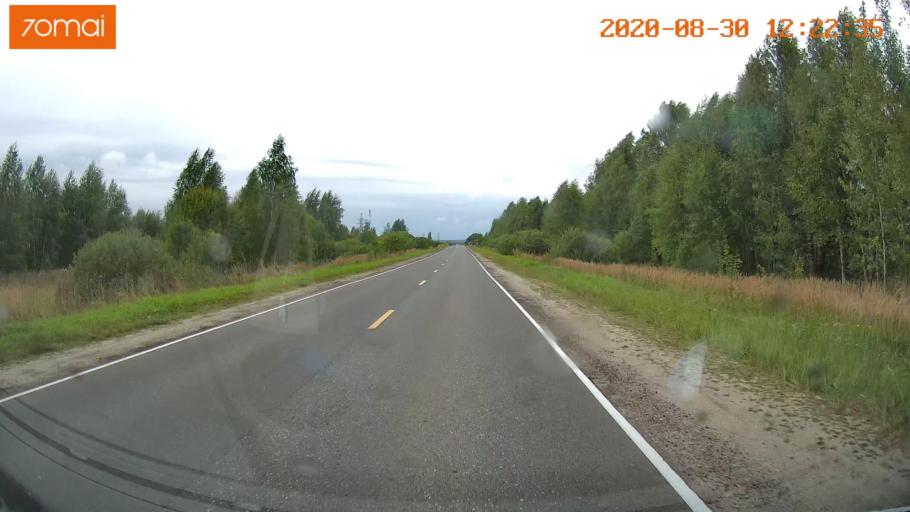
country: RU
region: Ivanovo
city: Yur'yevets
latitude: 57.3301
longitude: 42.8466
